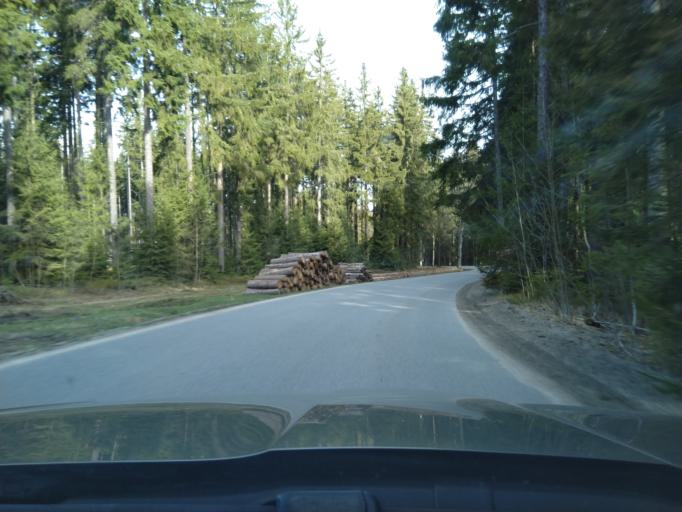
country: CZ
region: Jihocesky
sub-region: Okres Prachatice
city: Stachy
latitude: 49.0652
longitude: 13.6514
